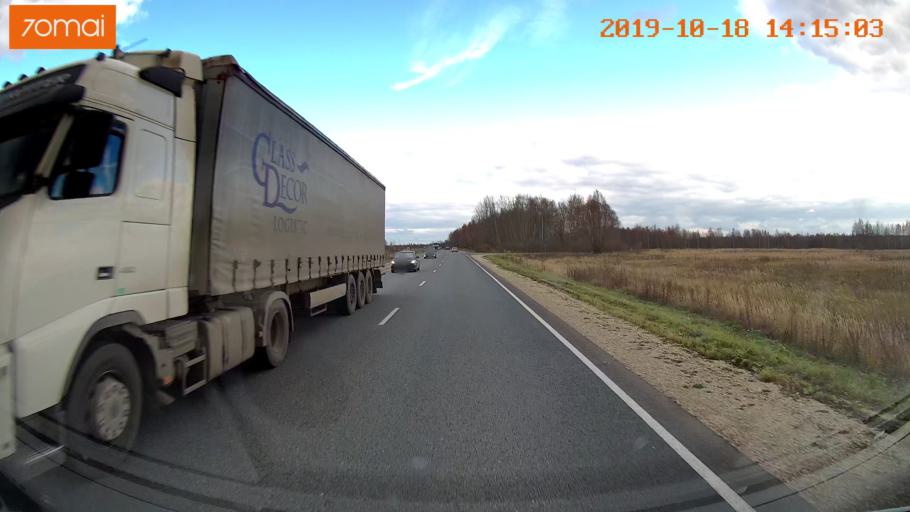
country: RU
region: Rjazan
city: Spas-Klepiki
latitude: 55.1469
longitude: 40.3085
